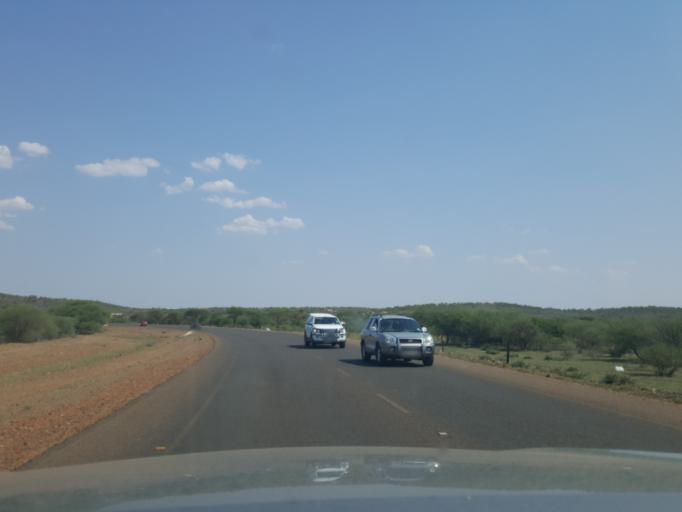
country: BW
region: South East
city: Ramotswa
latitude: -24.8586
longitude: 25.8307
